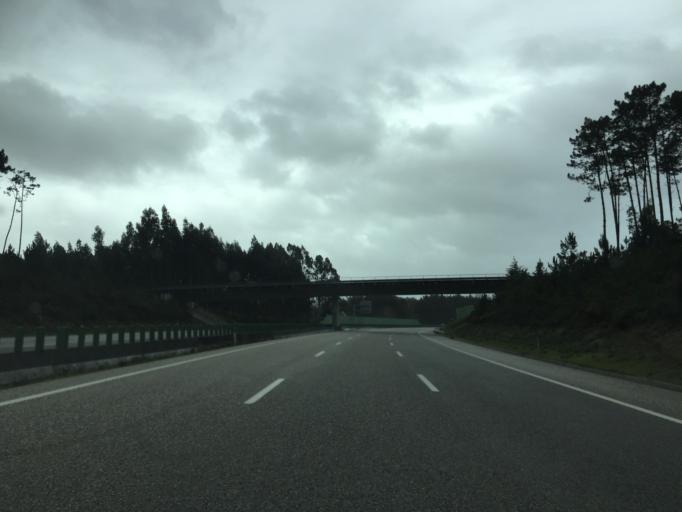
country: PT
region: Leiria
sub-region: Leiria
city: Monte Redondo
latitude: 39.9277
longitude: -8.7814
